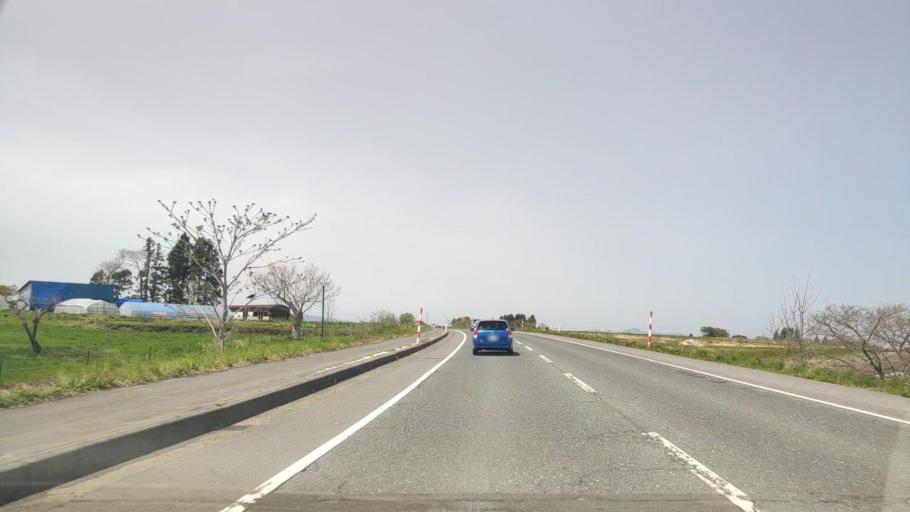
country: JP
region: Aomori
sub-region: Misawa Shi
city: Inuotose
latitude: 40.6366
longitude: 141.2422
